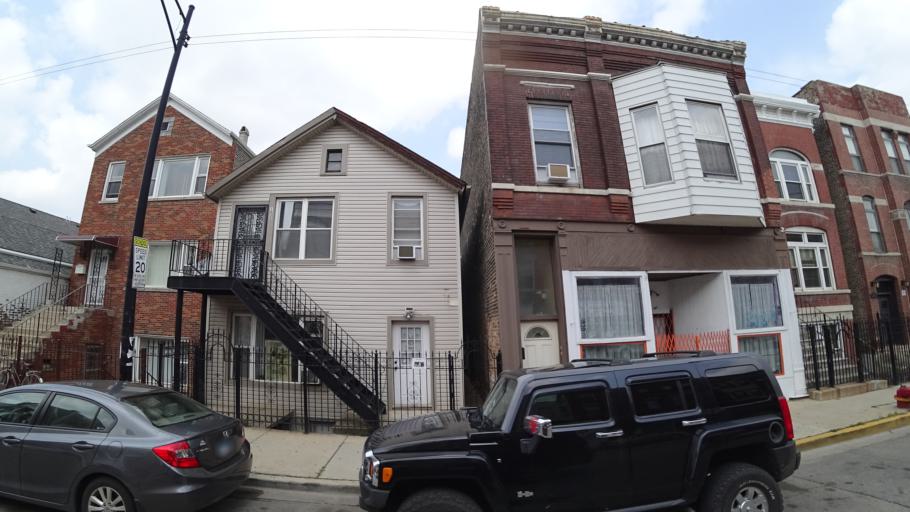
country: US
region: Illinois
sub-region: Cook County
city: Chicago
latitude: 41.8522
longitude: -87.6723
